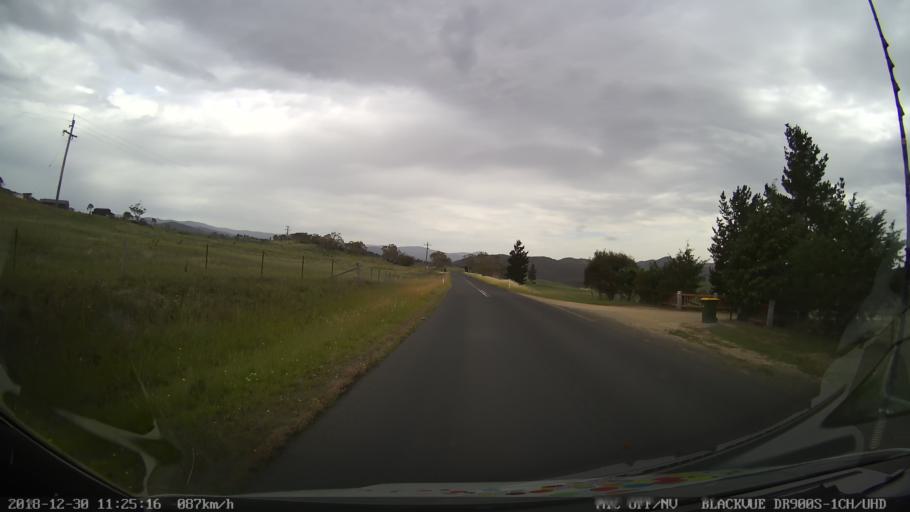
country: AU
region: New South Wales
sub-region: Snowy River
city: Jindabyne
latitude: -36.4734
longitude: 148.6483
